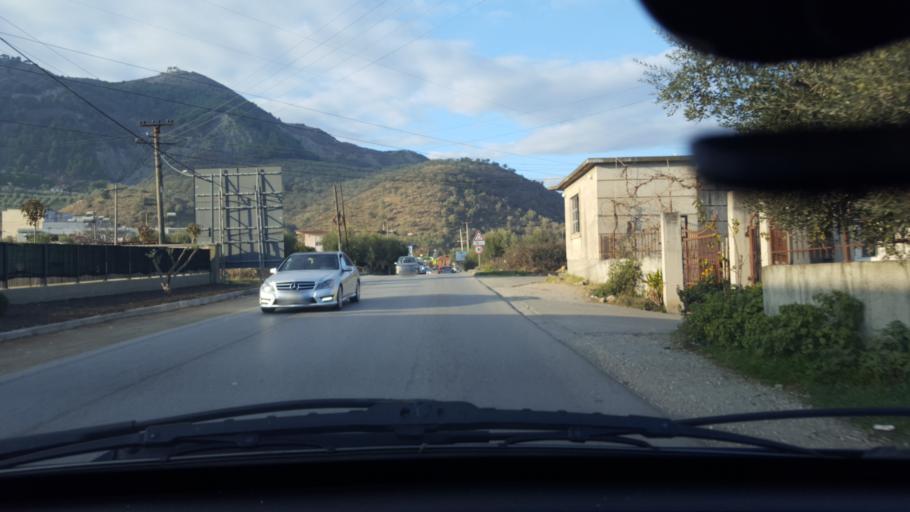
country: AL
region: Elbasan
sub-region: Rrethi i Elbasanit
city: Bradashesh
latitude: 41.1041
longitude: 20.0262
